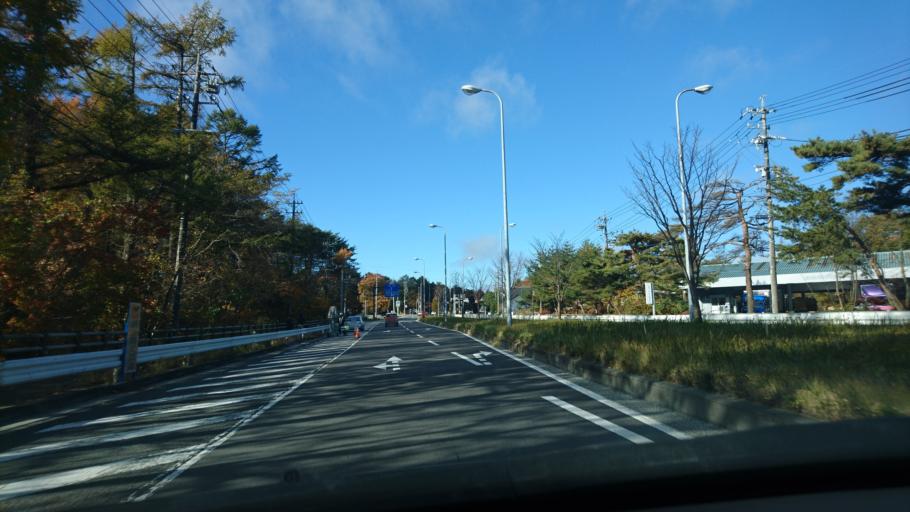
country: JP
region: Nagano
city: Saku
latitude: 36.3248
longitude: 138.6308
